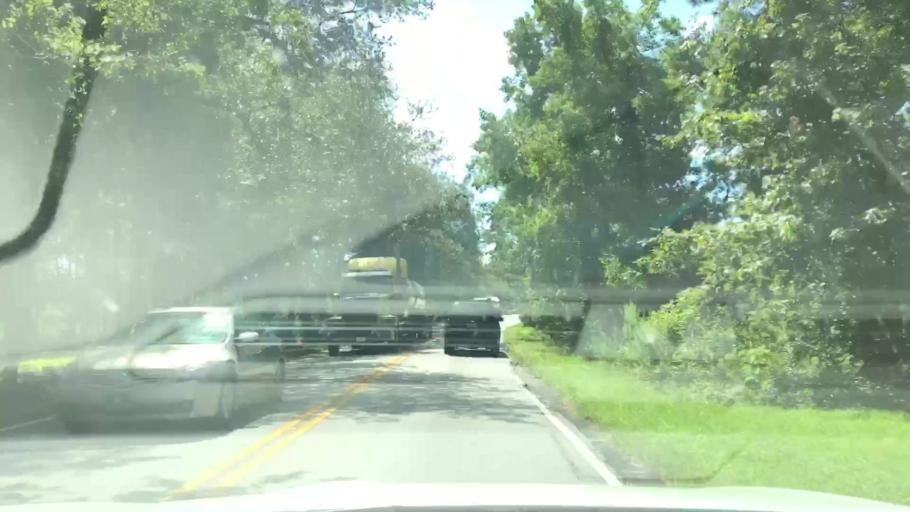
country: US
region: South Carolina
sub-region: Charleston County
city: Shell Point
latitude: 32.8376
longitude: -80.0494
